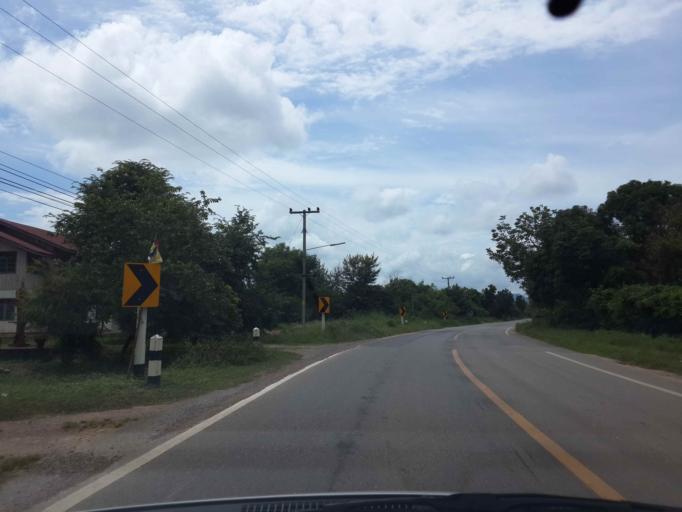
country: TH
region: Ratchaburi
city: Pak Tho
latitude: 13.3620
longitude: 99.7133
